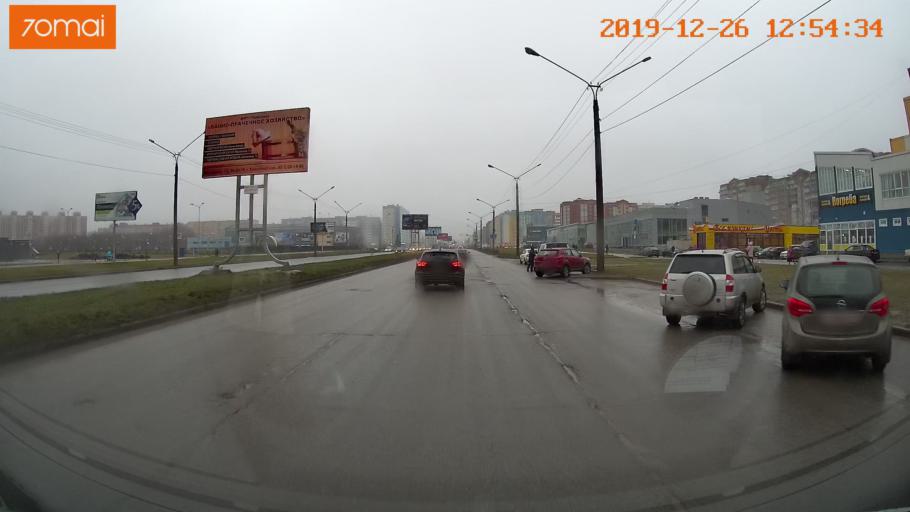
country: RU
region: Vologda
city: Cherepovets
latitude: 59.0920
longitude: 37.9152
